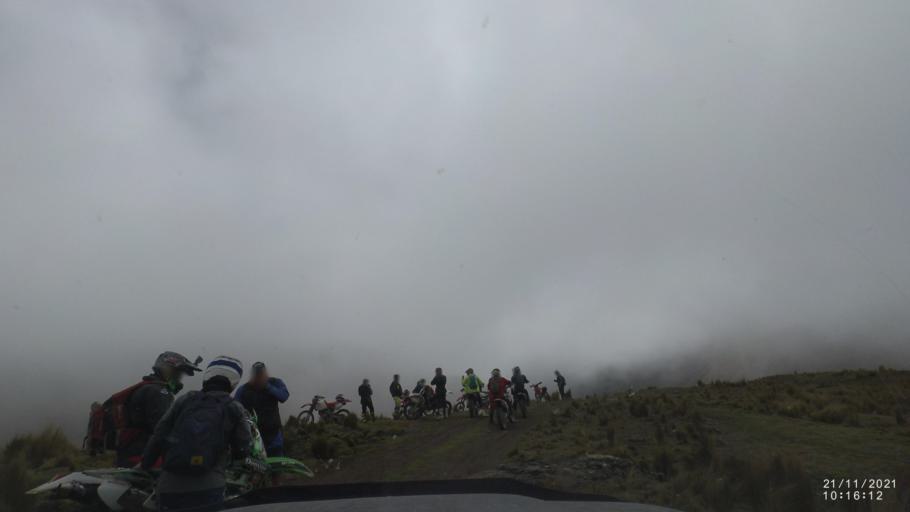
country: BO
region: Cochabamba
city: Cochabamba
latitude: -16.9920
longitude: -66.2676
